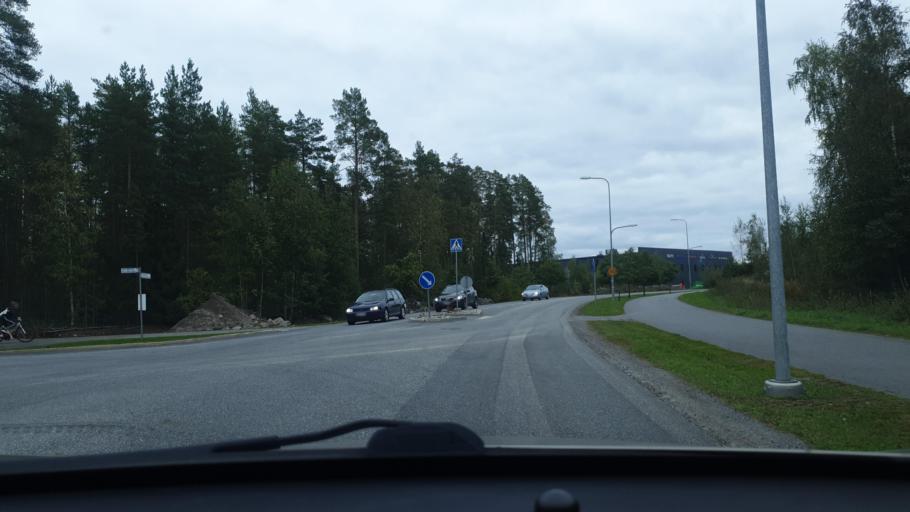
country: FI
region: Ostrobothnia
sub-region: Vaasa
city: Korsholm
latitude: 63.1195
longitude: 21.6566
